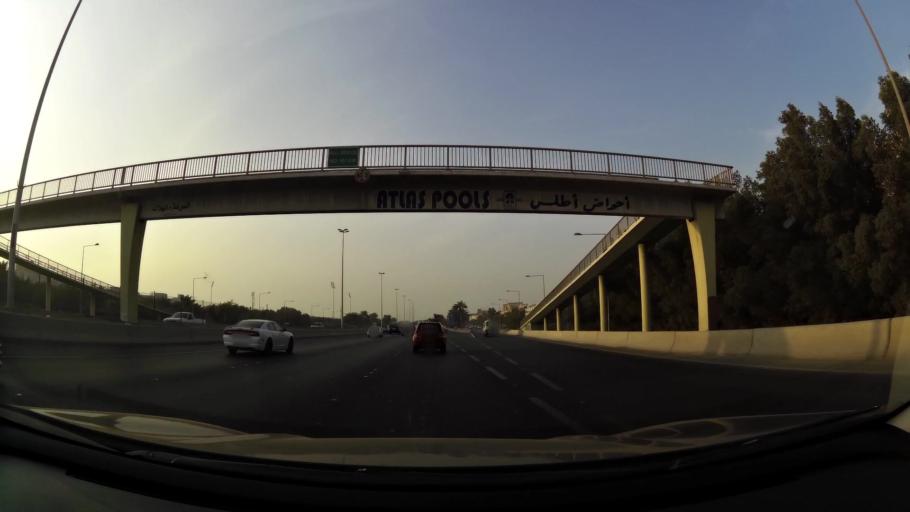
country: KW
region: Muhafazat Hawalli
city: Salwa
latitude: 29.2884
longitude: 48.0732
